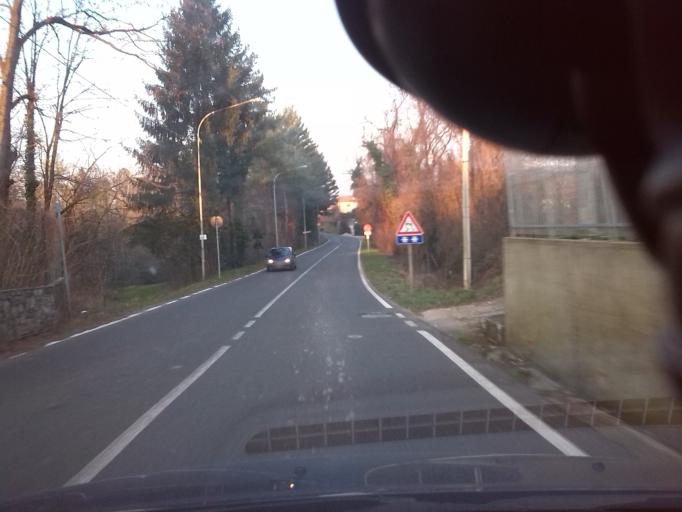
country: IT
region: Friuli Venezia Giulia
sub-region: Provincia di Udine
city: Cividale del Friuli
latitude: 46.0927
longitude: 13.4478
